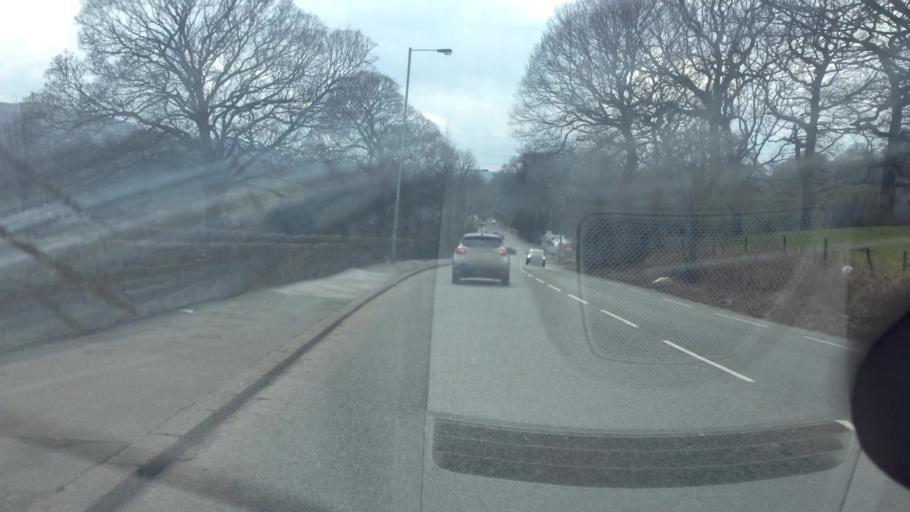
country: GB
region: England
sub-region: City and Borough of Leeds
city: Guiseley
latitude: 53.8575
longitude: -1.7382
